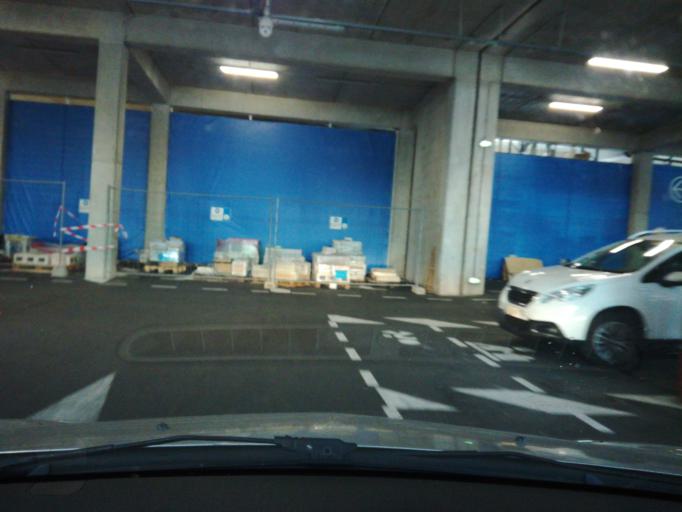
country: FR
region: Provence-Alpes-Cote d'Azur
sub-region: Departement des Alpes-Maritimes
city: Vallauris
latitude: 43.6013
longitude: 7.0707
